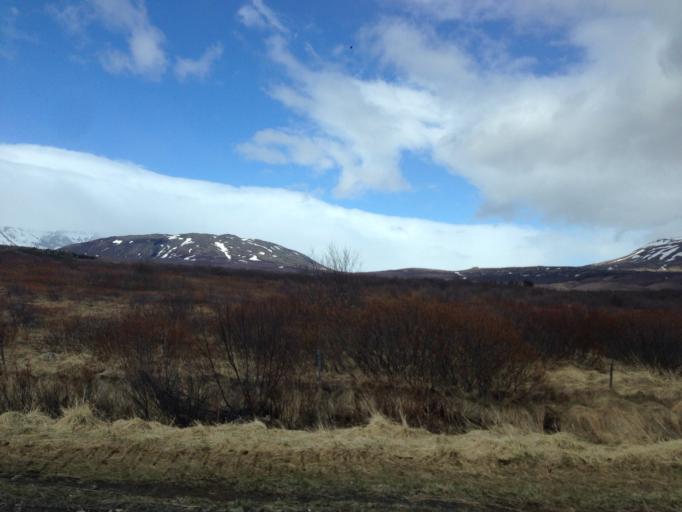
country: IS
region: South
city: Selfoss
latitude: 64.2769
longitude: -20.4275
